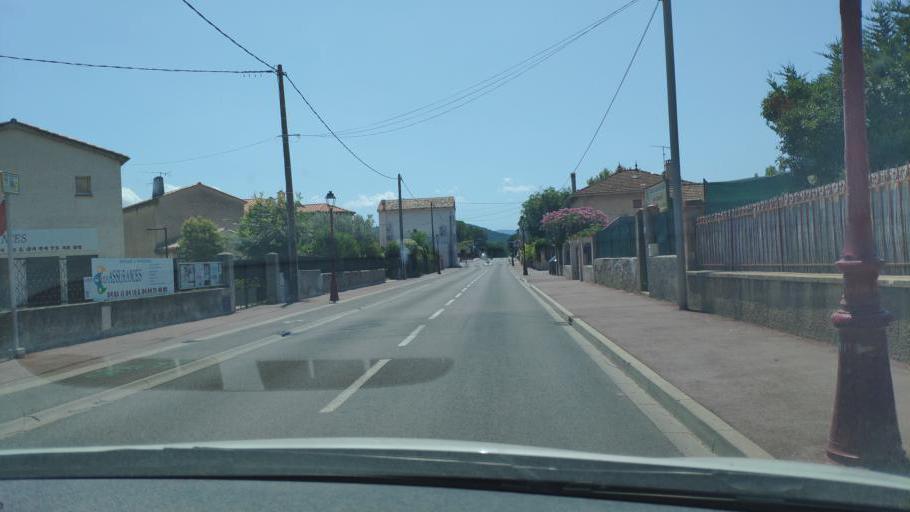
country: FR
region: Provence-Alpes-Cote d'Azur
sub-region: Departement du Var
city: Les Arcs
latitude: 43.4566
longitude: 6.4803
